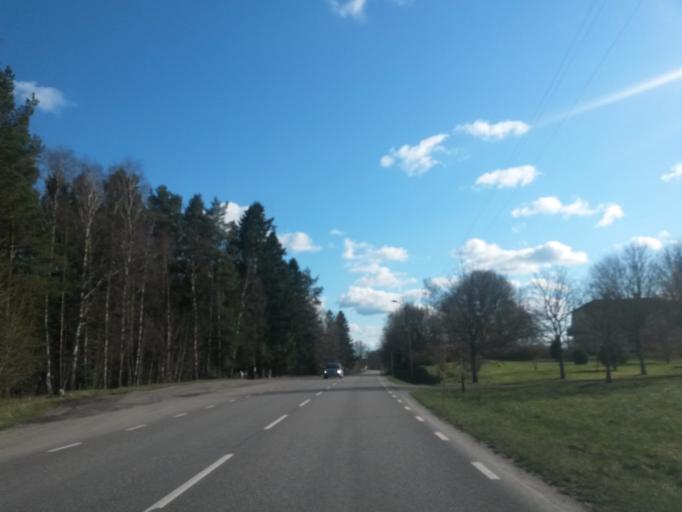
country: SE
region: Vaestra Goetaland
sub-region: Vargarda Kommun
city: Vargarda
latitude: 58.0473
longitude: 12.8155
